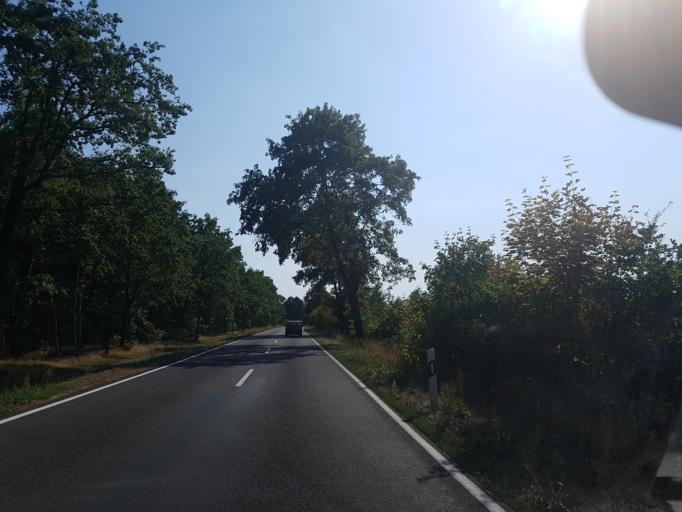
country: DE
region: Saxony-Anhalt
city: Annaburg
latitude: 51.7102
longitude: 13.0243
